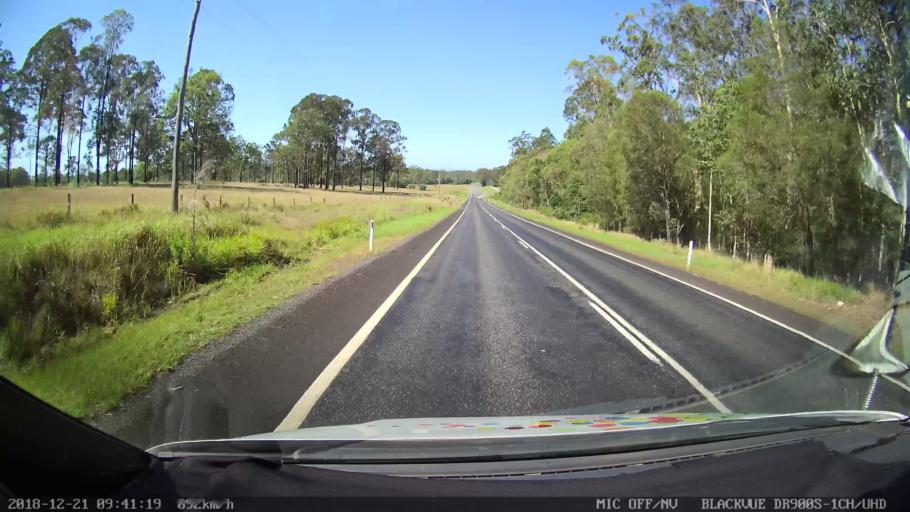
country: AU
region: New South Wales
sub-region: Clarence Valley
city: Grafton
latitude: -29.5838
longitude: 152.9583
